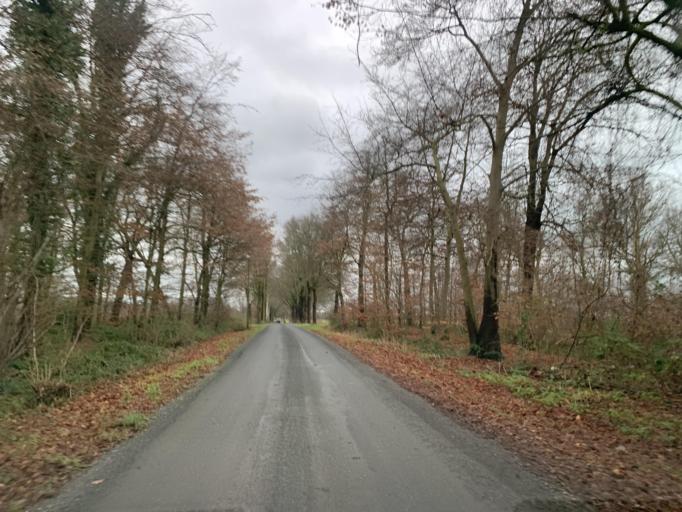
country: DE
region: North Rhine-Westphalia
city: Olfen
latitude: 51.7590
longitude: 7.3566
